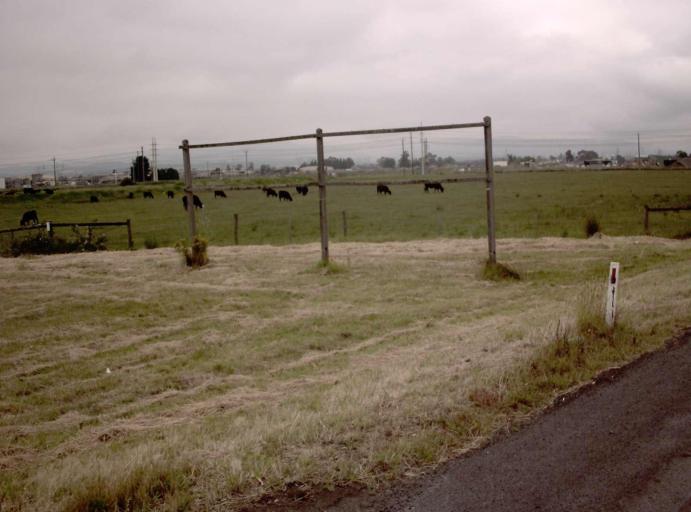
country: AU
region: Victoria
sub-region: Latrobe
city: Morwell
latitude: -38.2515
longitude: 146.4259
